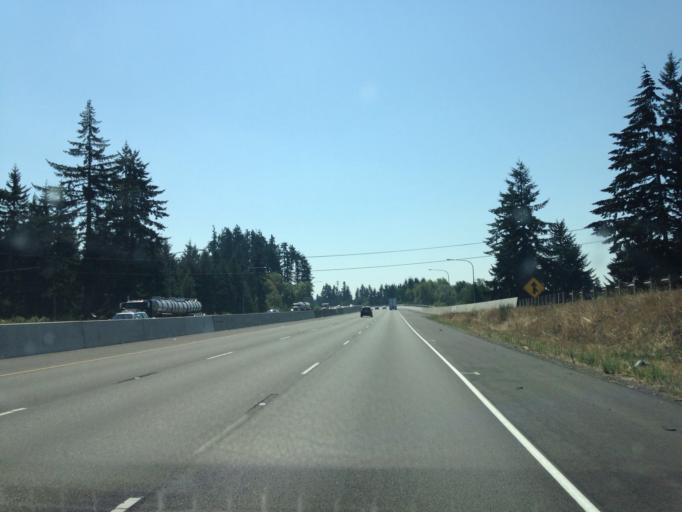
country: US
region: Washington
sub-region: Thurston County
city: Grand Mound
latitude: 46.8011
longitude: -123.0081
